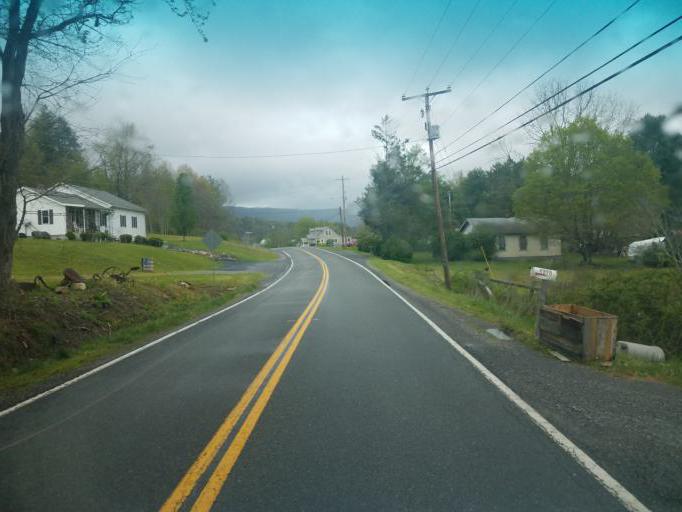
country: US
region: Virginia
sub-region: Bland County
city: Bland
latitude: 37.1670
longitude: -81.1460
